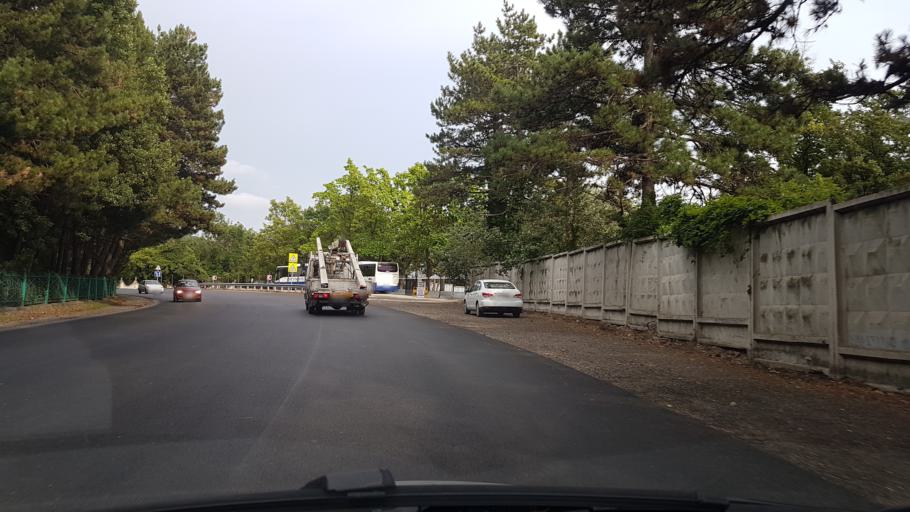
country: RU
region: Krasnodarskiy
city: Lermontovo
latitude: 44.2741
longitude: 38.8020
